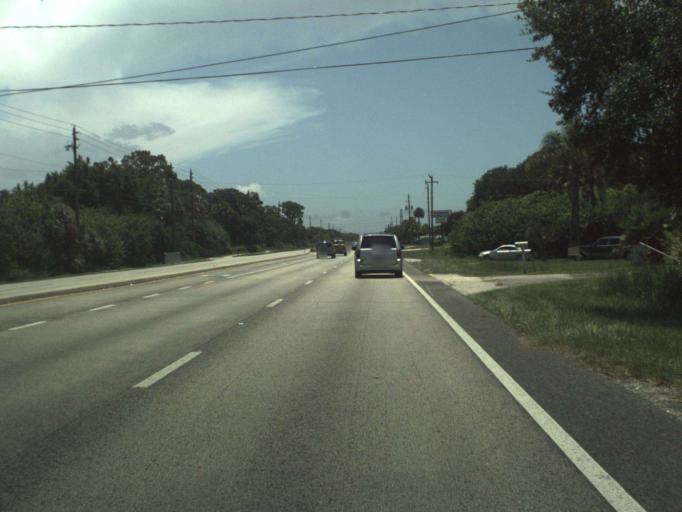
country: US
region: Florida
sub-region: Indian River County
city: Sebastian
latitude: 27.7854
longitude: -80.4539
